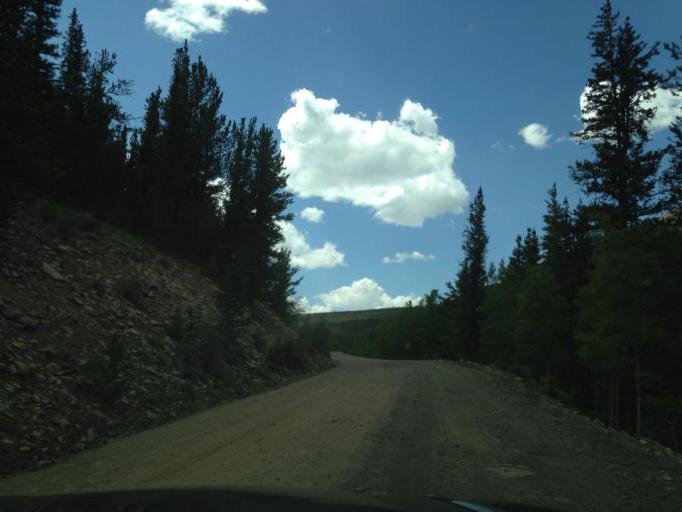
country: US
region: Colorado
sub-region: Park County
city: Fairplay
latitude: 39.3461
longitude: -105.9273
